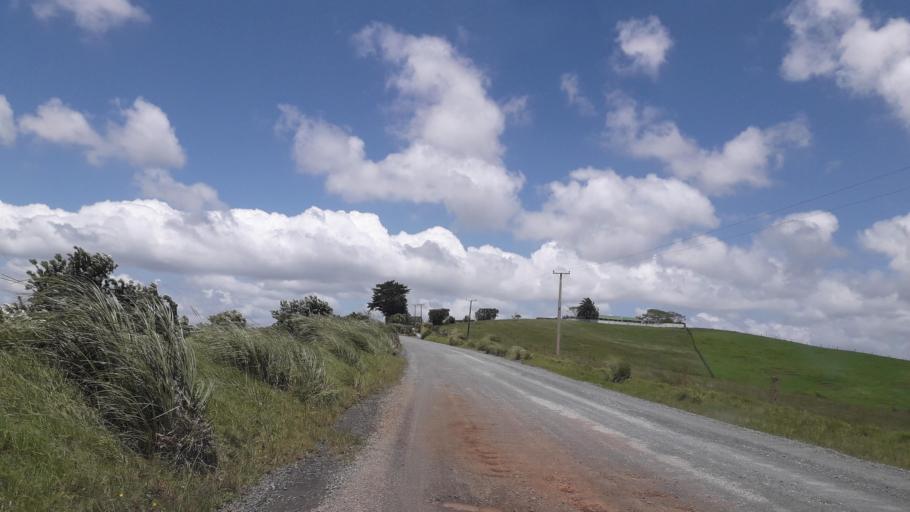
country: NZ
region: Northland
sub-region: Far North District
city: Taipa
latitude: -34.9990
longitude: 173.4300
